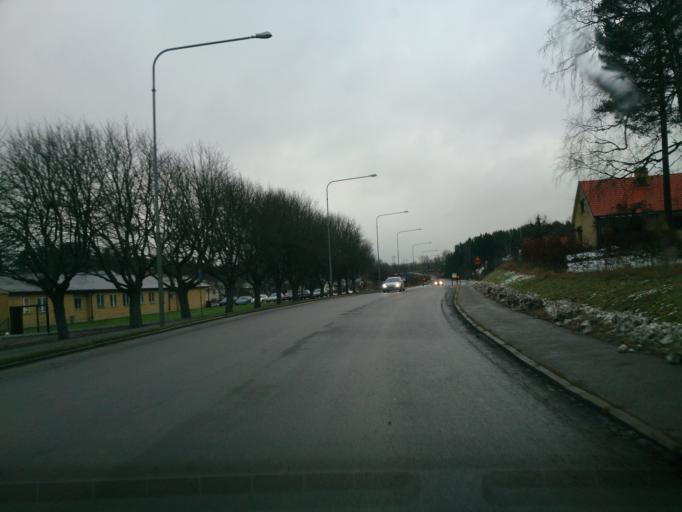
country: SE
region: OEstergoetland
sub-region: Atvidabergs Kommun
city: Atvidaberg
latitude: 58.2071
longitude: 16.0081
